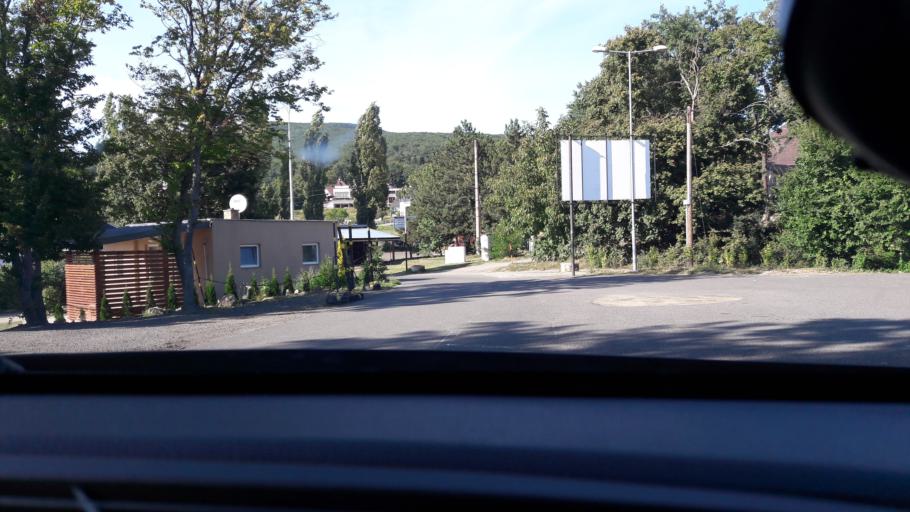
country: SK
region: Kosicky
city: Vinne
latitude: 48.8081
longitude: 22.0116
